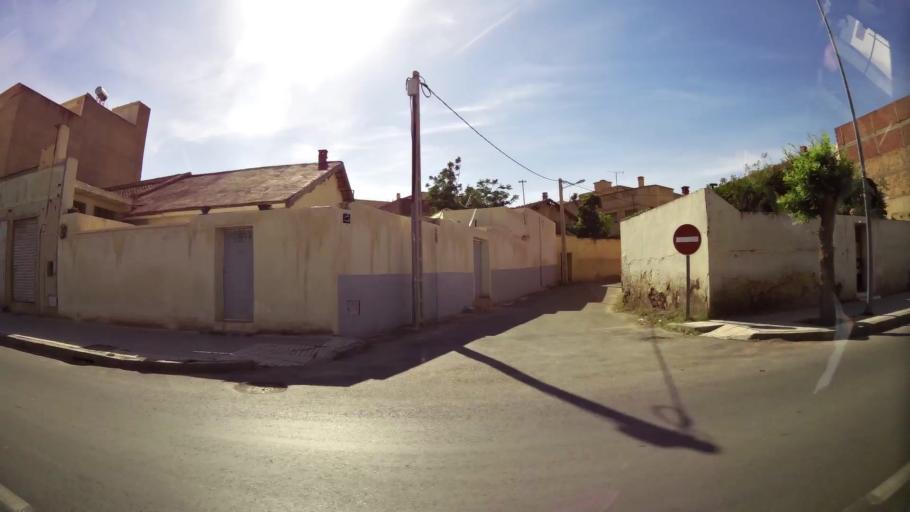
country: MA
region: Oriental
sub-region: Oujda-Angad
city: Oujda
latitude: 34.6675
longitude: -1.9128
